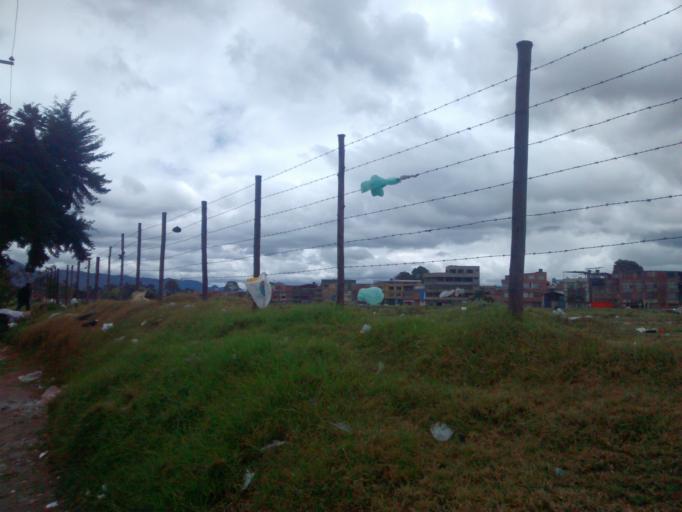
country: CO
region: Cundinamarca
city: Cota
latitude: 4.7388
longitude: -74.1055
